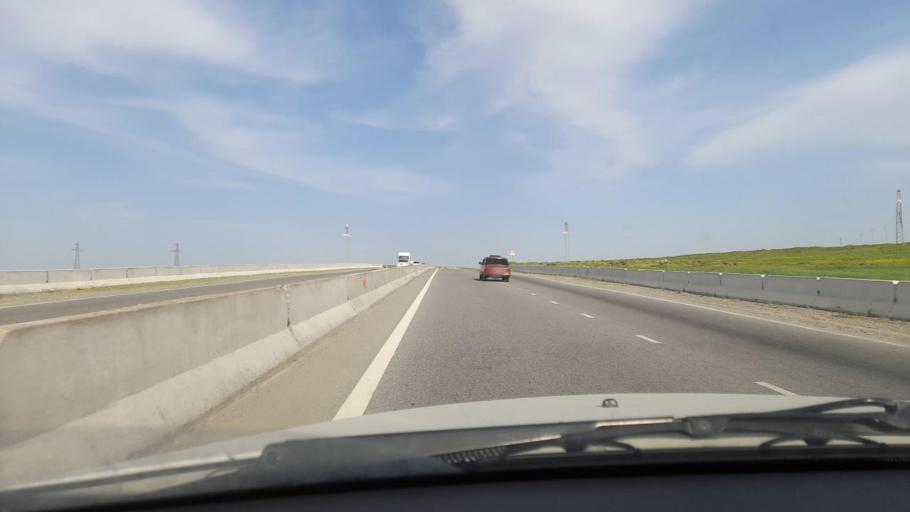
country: UZ
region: Jizzax
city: Jizzax
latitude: 40.0540
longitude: 67.7251
